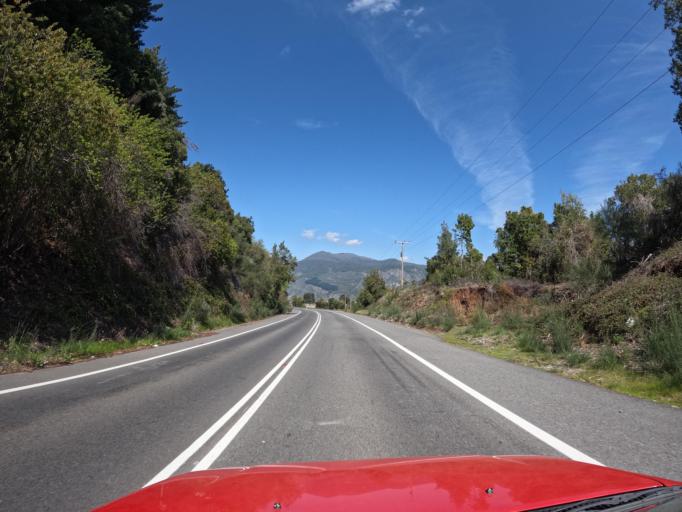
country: CL
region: Maule
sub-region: Provincia de Linares
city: Colbun
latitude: -35.6992
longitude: -71.2243
